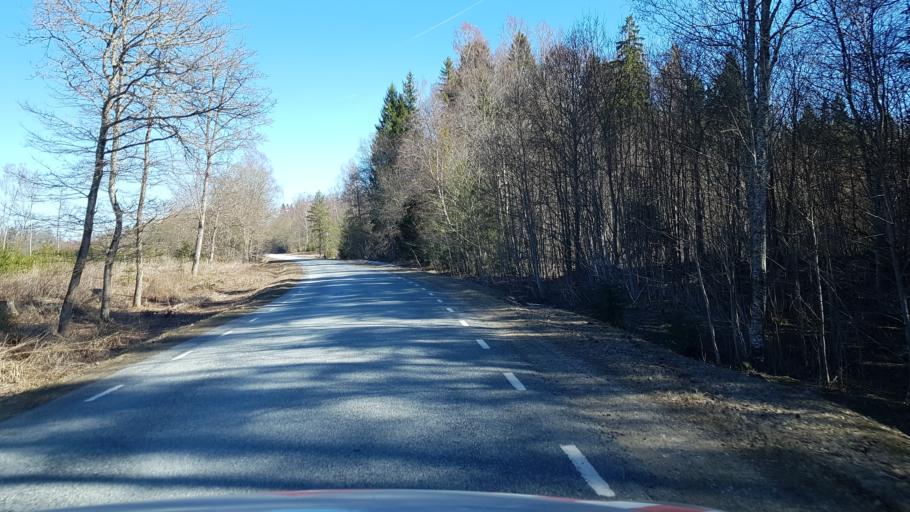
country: EE
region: Laeaene-Virumaa
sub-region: Someru vald
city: Someru
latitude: 59.3308
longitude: 26.5851
